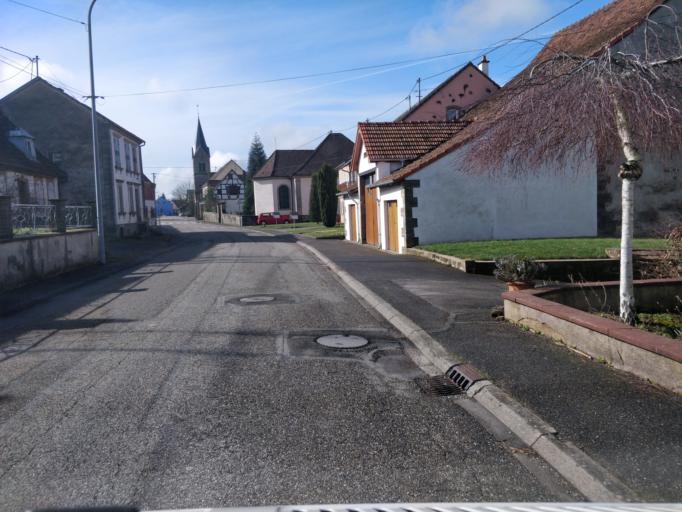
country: FR
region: Alsace
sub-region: Departement du Bas-Rhin
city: Drulingen
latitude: 48.8930
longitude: 7.2549
